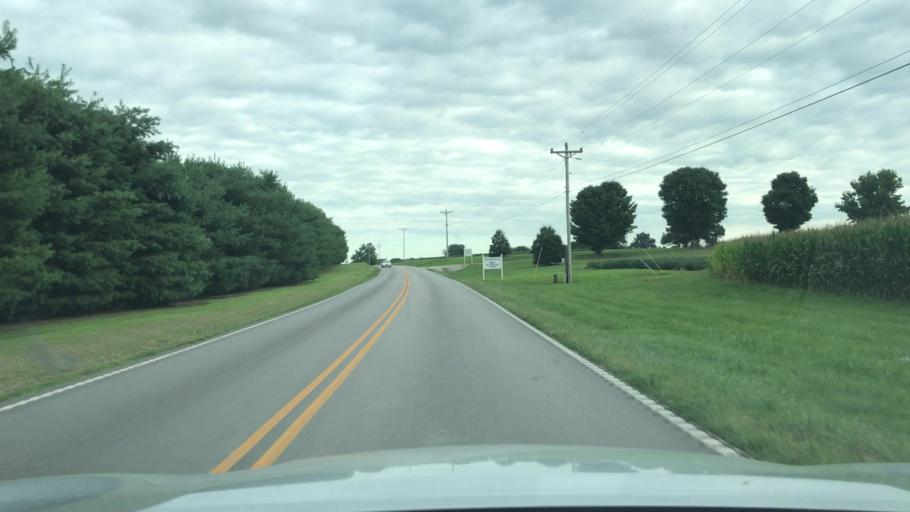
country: US
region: Kentucky
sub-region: Todd County
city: Guthrie
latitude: 36.6703
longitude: -87.1977
